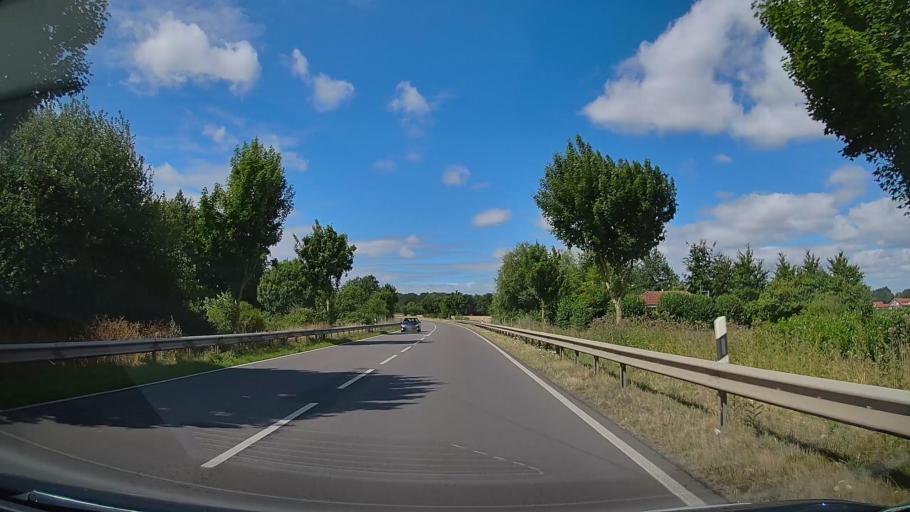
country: DE
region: Lower Saxony
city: Vechta
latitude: 52.7535
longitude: 8.2713
